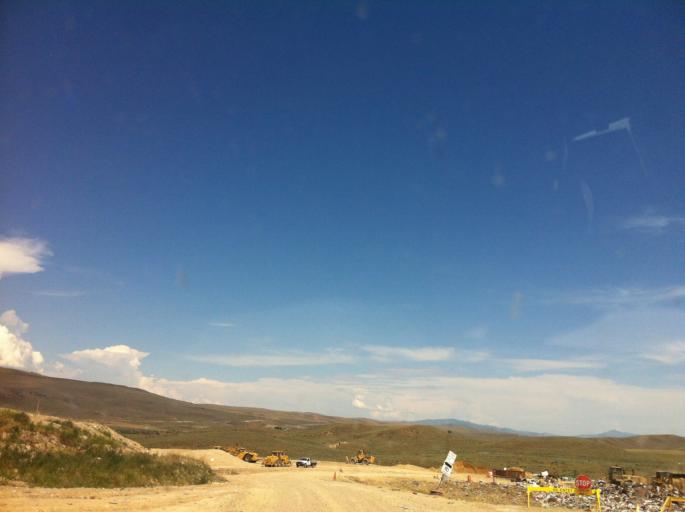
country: US
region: Oregon
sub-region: Baker County
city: Baker City
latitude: 44.7049
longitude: -117.7873
